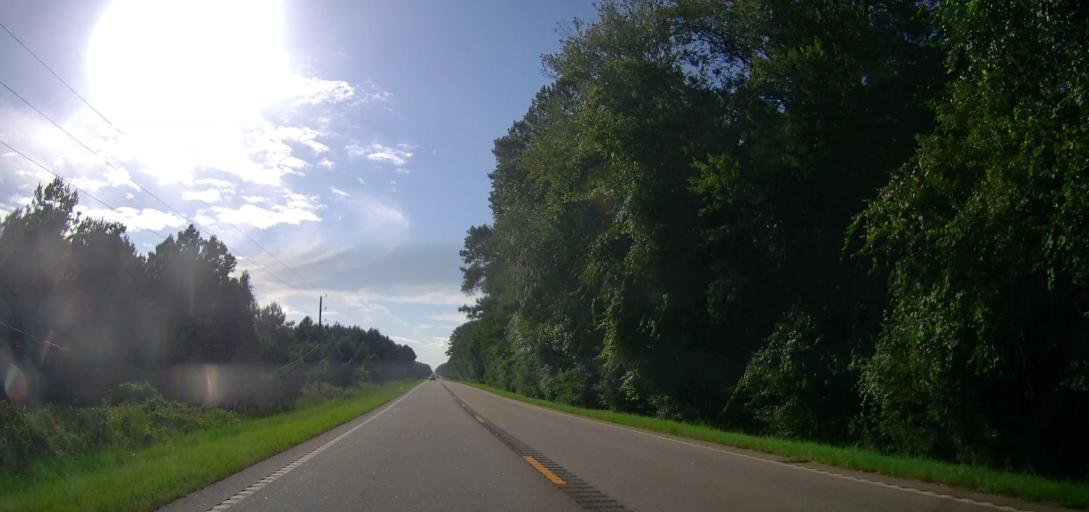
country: US
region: Georgia
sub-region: Coffee County
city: Douglas
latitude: 31.4651
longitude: -82.7583
